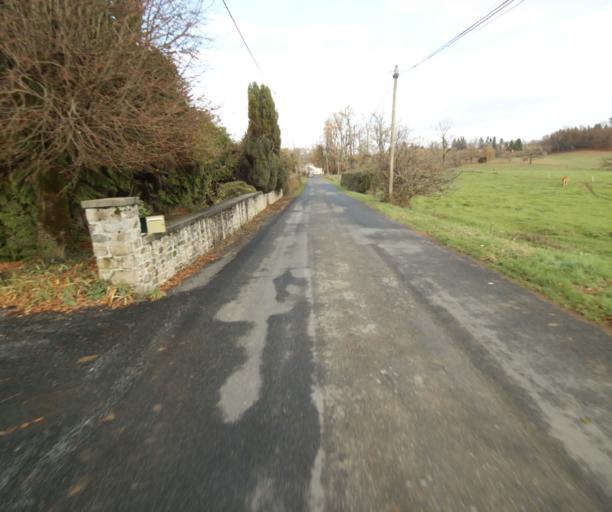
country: FR
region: Limousin
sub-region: Departement de la Correze
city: Sainte-Fereole
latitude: 45.2718
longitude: 1.6027
